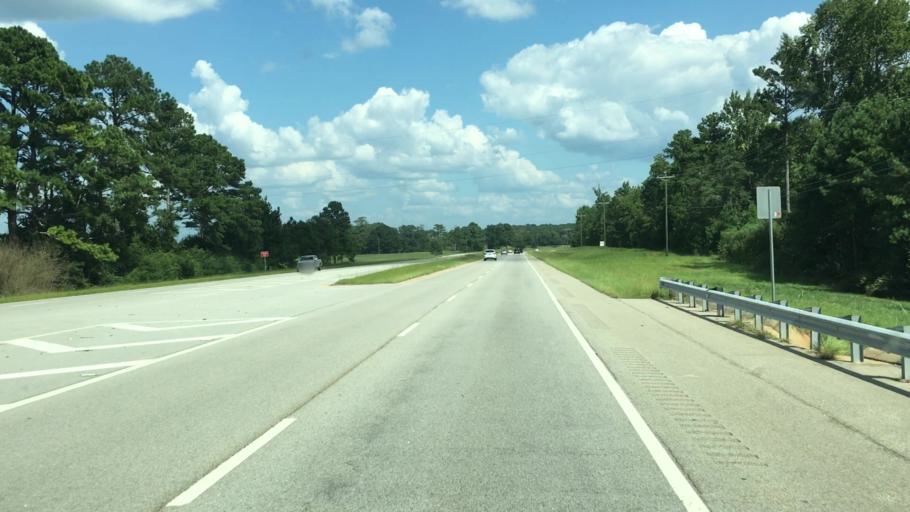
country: US
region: Georgia
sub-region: Putnam County
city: Eatonton
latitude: 33.2728
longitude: -83.3553
